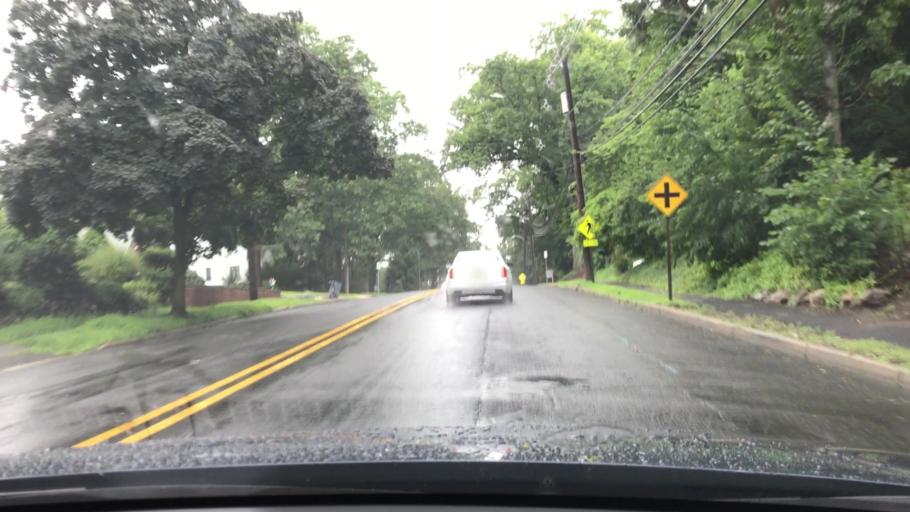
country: US
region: New Jersey
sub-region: Bergen County
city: Oradell
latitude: 40.9566
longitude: -74.0403
